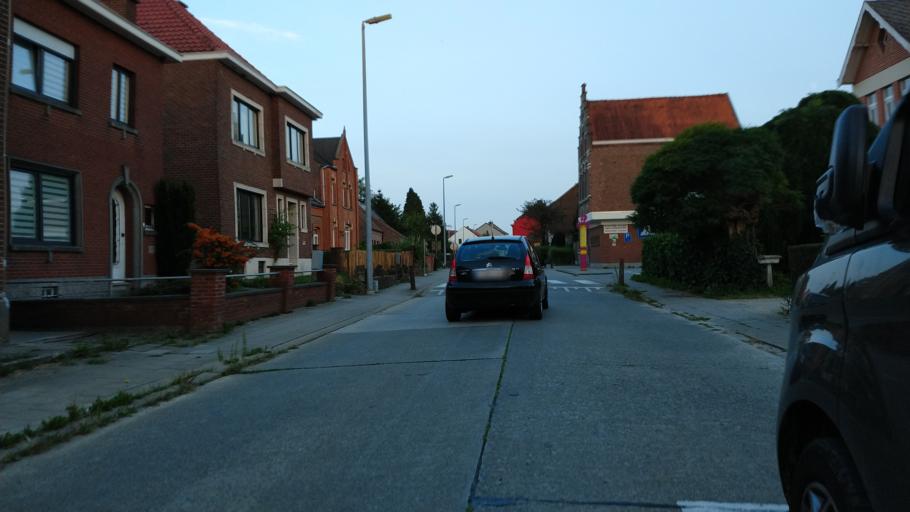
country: BE
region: Flanders
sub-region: Provincie Vlaams-Brabant
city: Bierbeek
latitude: 50.8522
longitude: 4.7845
